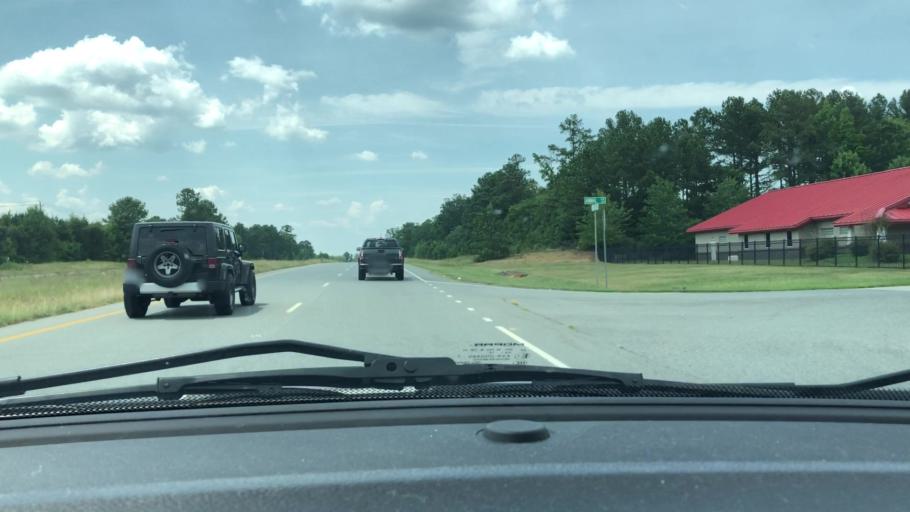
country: US
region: North Carolina
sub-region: Chatham County
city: Farmville
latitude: 35.5232
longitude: -79.2249
